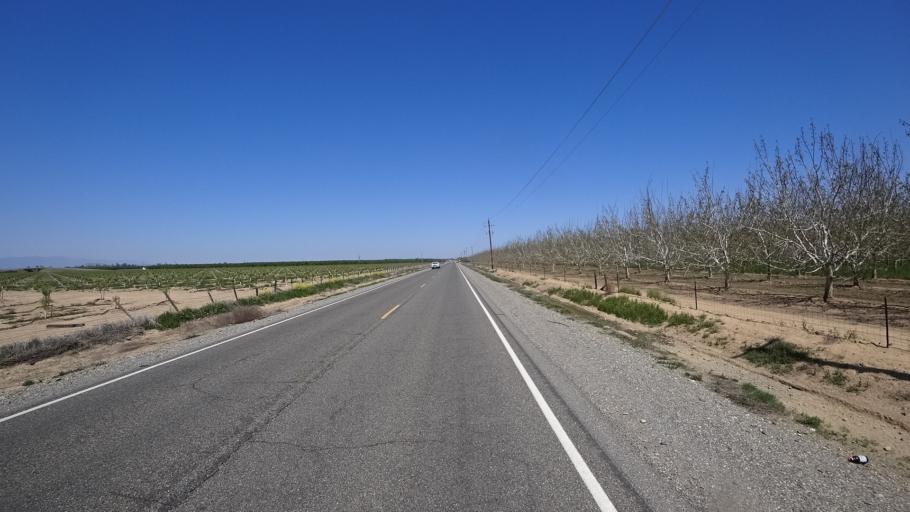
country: US
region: California
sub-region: Glenn County
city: Orland
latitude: 39.6639
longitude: -122.1970
